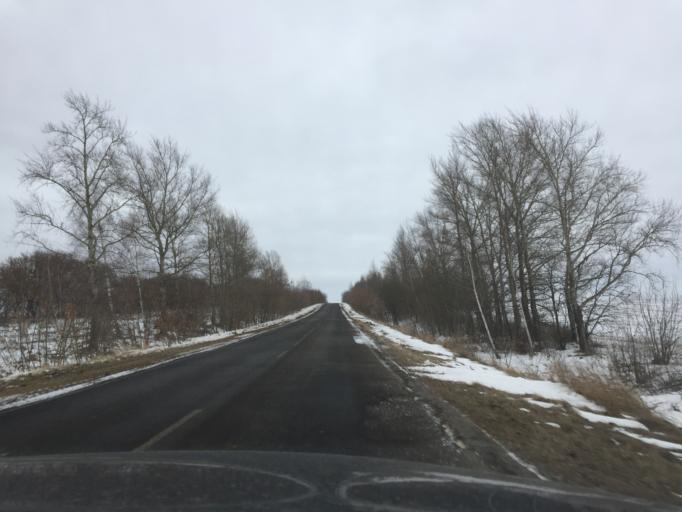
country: RU
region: Tula
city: Shchekino
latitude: 53.8225
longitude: 37.5232
